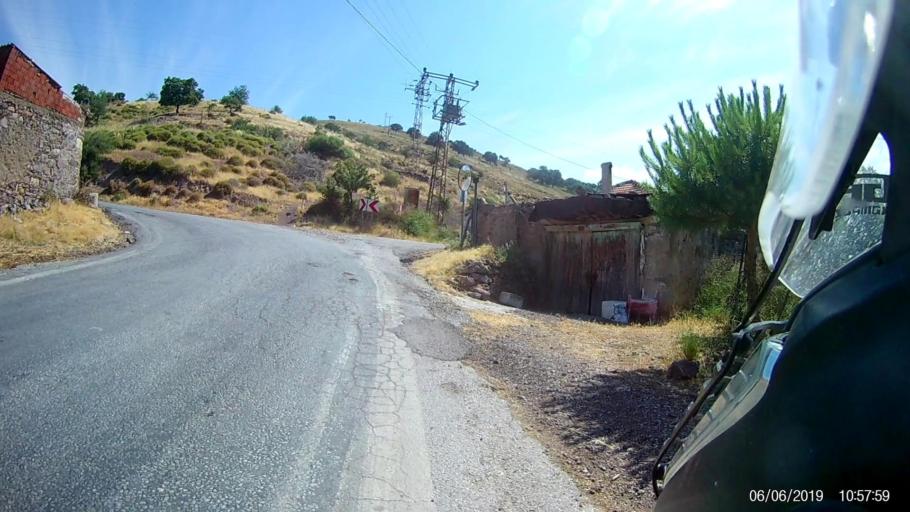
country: TR
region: Istanbul
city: Sancaktepe
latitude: 41.0363
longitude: 29.2608
